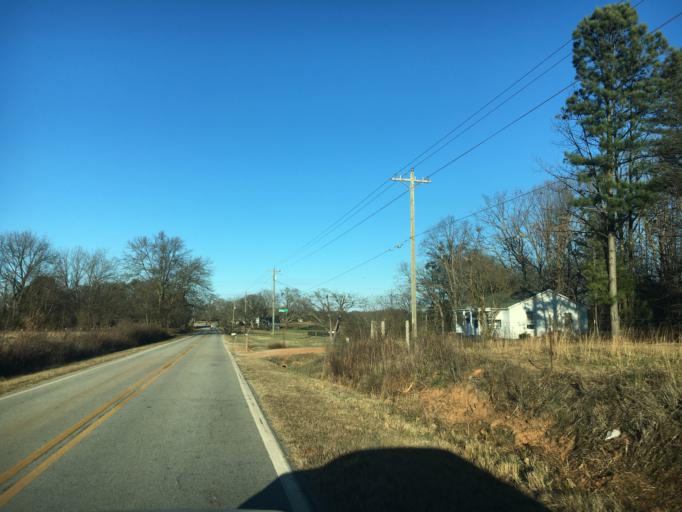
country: US
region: Georgia
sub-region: Franklin County
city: Lavonia
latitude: 34.3747
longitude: -83.0292
